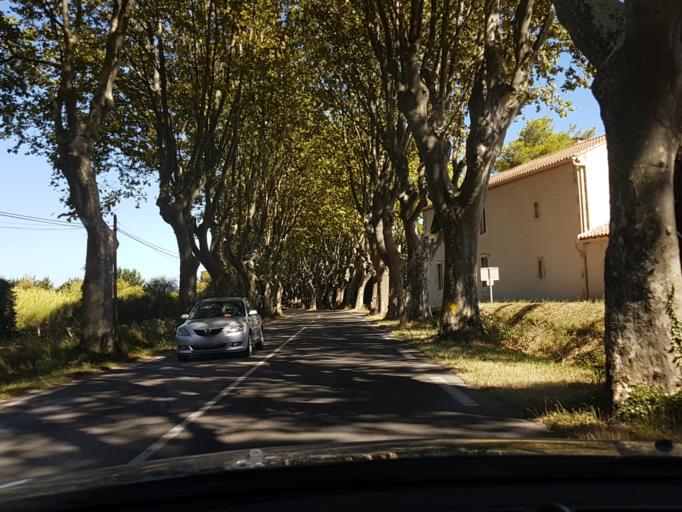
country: FR
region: Provence-Alpes-Cote d'Azur
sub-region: Departement des Bouches-du-Rhone
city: Saint-Remy-de-Provence
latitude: 43.7846
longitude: 4.8741
